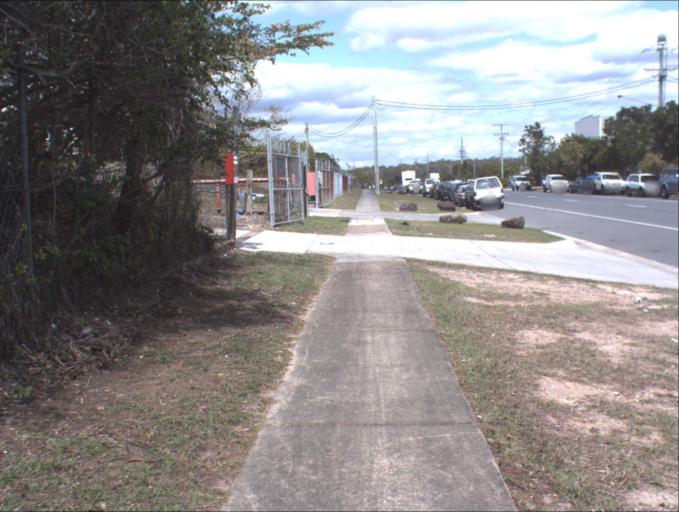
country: AU
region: Queensland
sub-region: Logan
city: Logan Reserve
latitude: -27.6834
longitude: 153.0706
